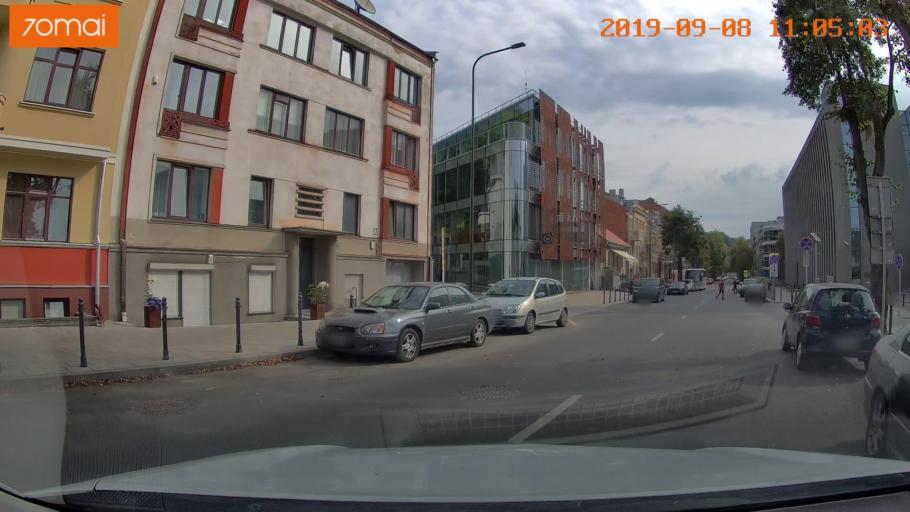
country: LT
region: Kauno apskritis
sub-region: Kaunas
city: Kaunas
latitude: 54.9007
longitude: 23.9125
